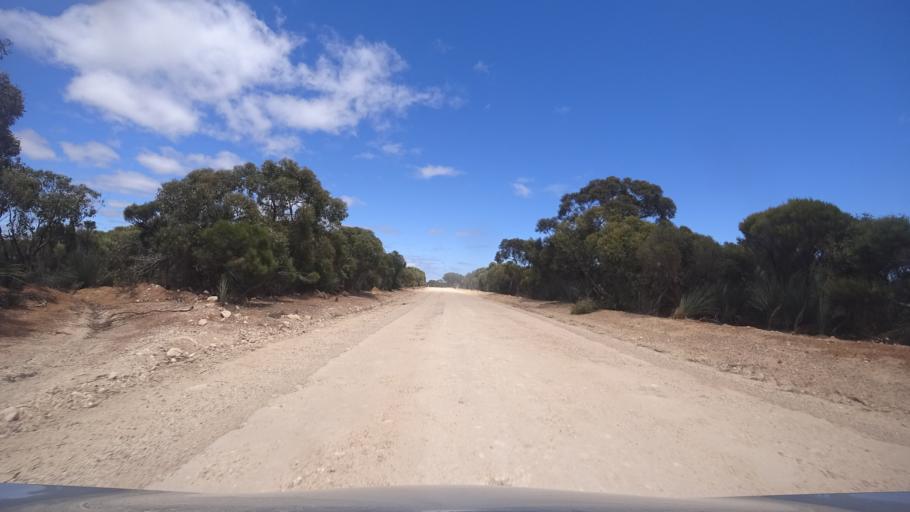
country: AU
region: South Australia
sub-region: Kangaroo Island
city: Kingscote
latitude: -35.6368
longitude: 137.2443
